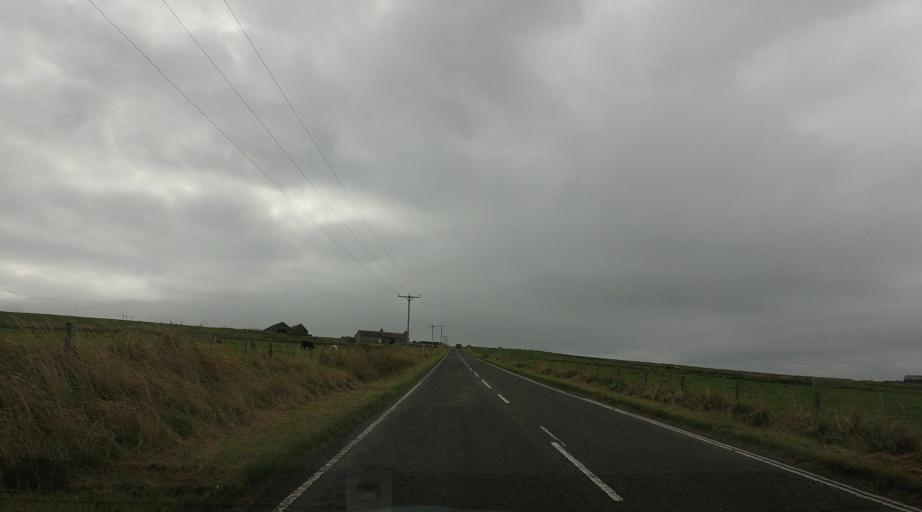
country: GB
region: Scotland
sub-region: Orkney Islands
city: Orkney
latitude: 58.7818
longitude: -2.9592
